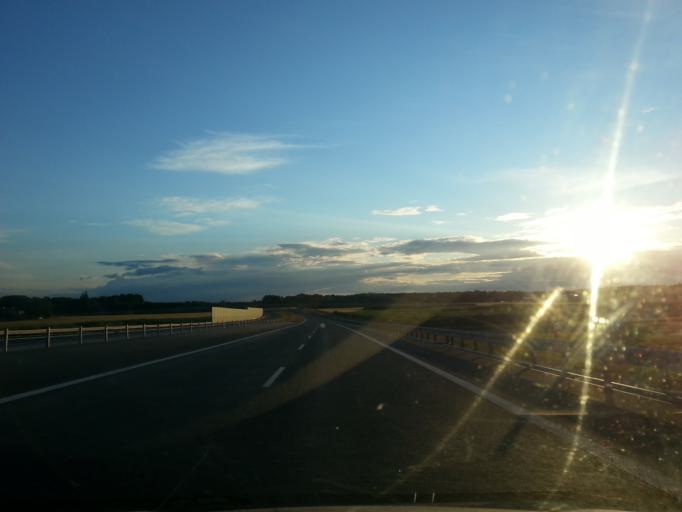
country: PL
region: Greater Poland Voivodeship
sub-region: Powiat kepinski
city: Kepno
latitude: 51.3172
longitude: 17.9887
